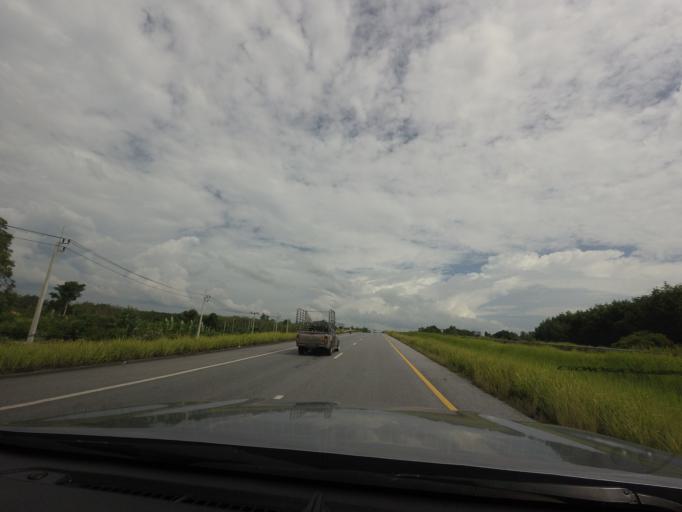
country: TH
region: Pattani
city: Mae Lan
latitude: 6.6861
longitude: 101.2315
